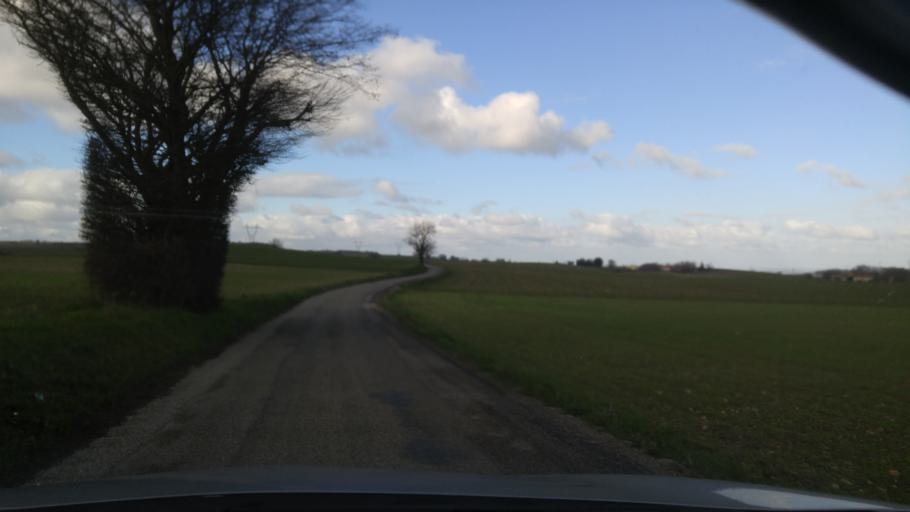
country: FR
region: Rhone-Alpes
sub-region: Departement de l'Isere
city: Roche
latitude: 45.5732
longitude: 5.1820
